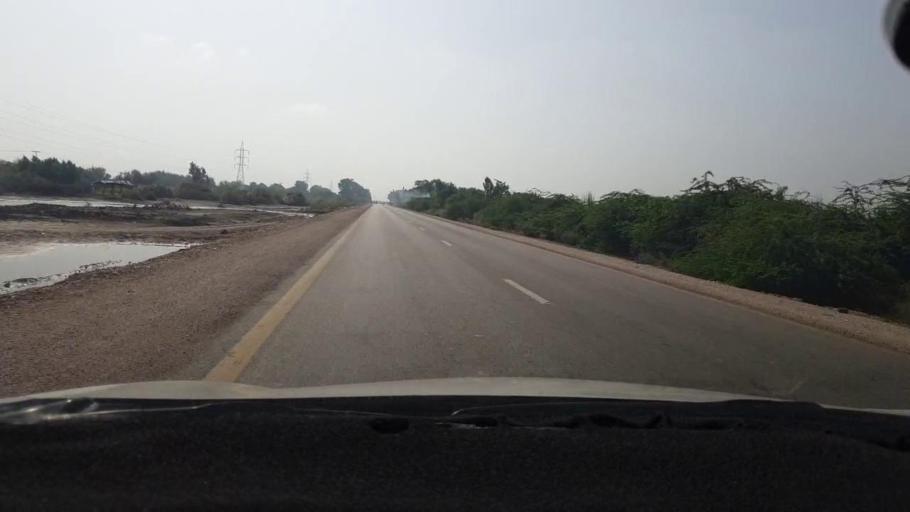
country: PK
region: Sindh
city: Jhol
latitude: 25.9073
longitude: 69.0166
